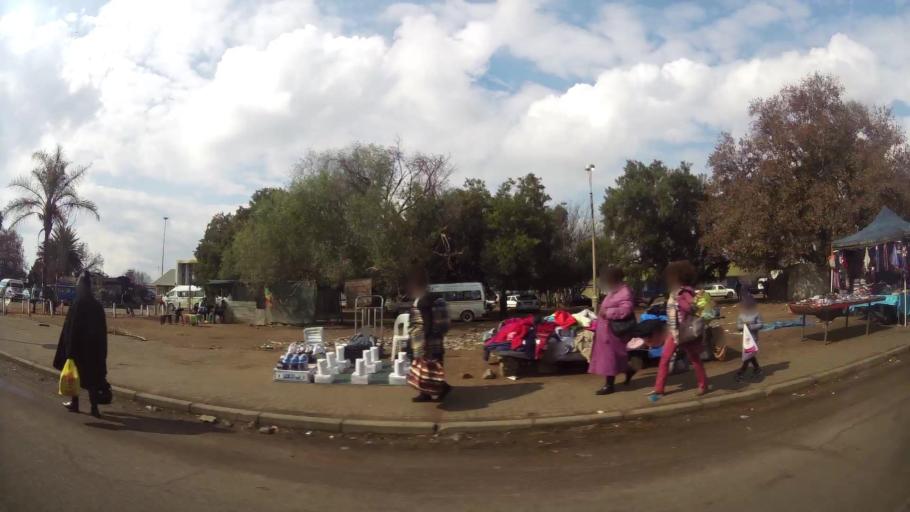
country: ZA
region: Gauteng
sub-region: Sedibeng District Municipality
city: Vereeniging
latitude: -26.6745
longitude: 27.9339
